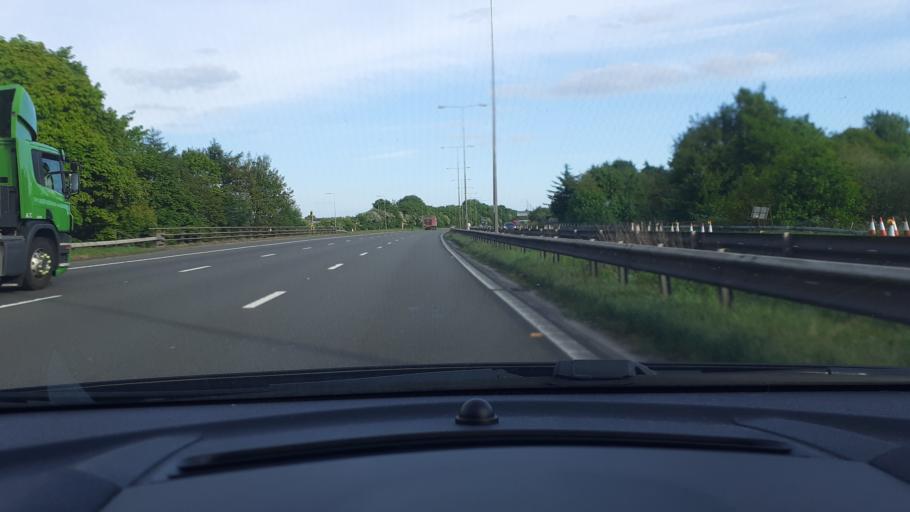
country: GB
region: England
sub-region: Borough of Wigan
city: Ashton in Makerfield
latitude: 53.5063
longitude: -2.6648
